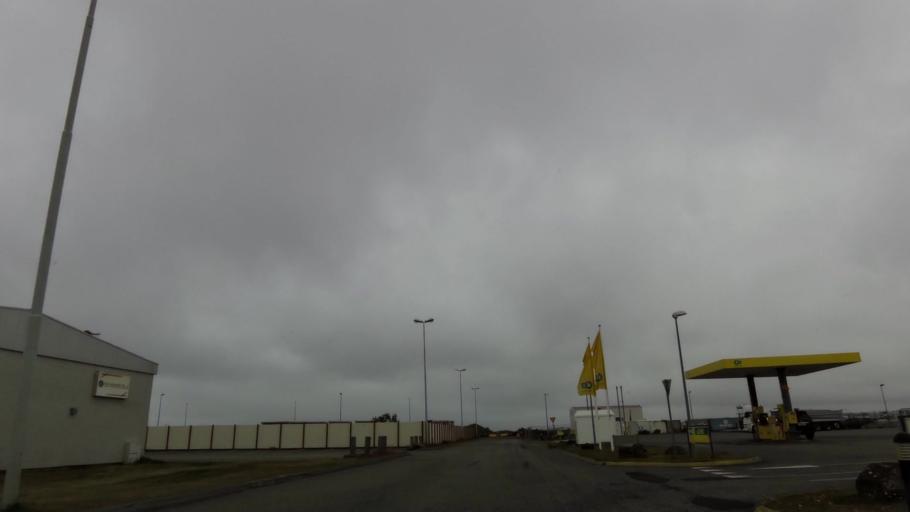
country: IS
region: Southern Peninsula
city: Reykjanesbaer
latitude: 63.9801
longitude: -22.5479
